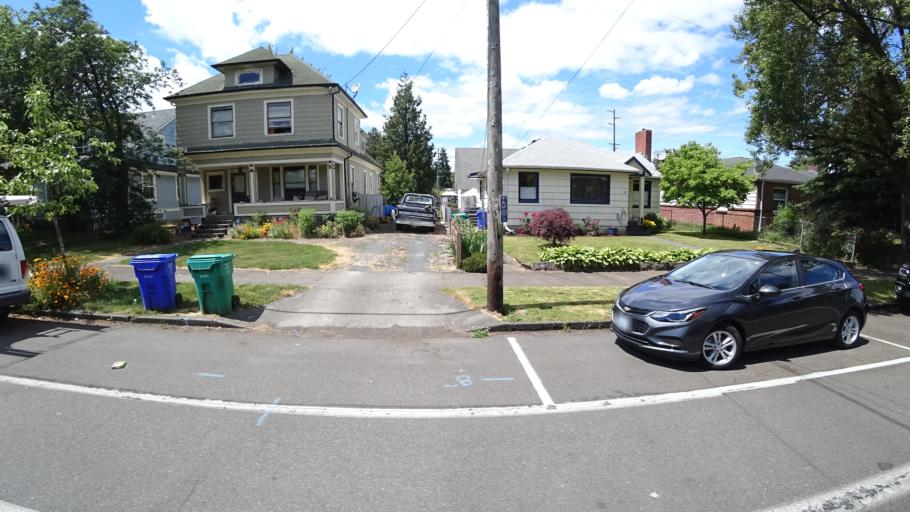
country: US
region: Oregon
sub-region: Multnomah County
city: Portland
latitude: 45.5842
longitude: -122.7228
